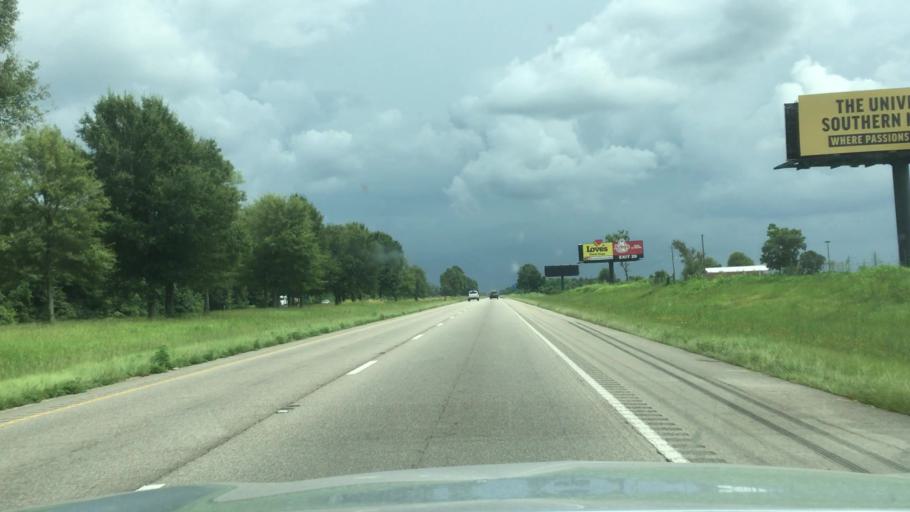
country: US
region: Mississippi
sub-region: Pearl River County
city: Carriere
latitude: 30.5772
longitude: -89.6308
